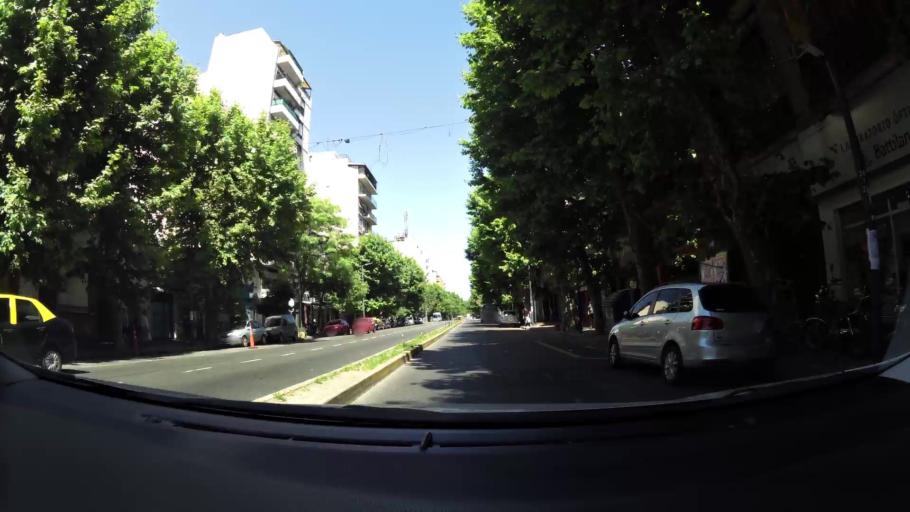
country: AR
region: Buenos Aires F.D.
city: Buenos Aires
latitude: -34.6363
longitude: -58.4009
